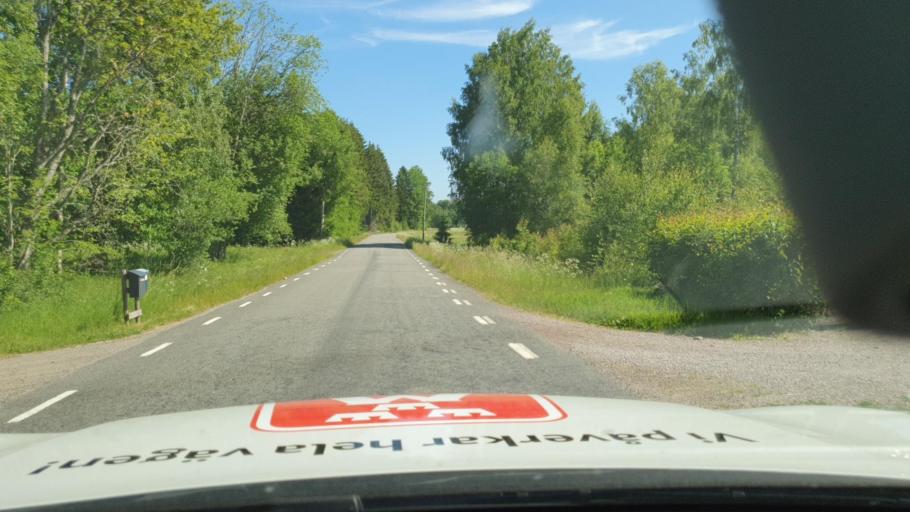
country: SE
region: Vaestra Goetaland
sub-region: Tidaholms Kommun
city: Olofstorp
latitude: 58.2844
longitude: 14.0135
